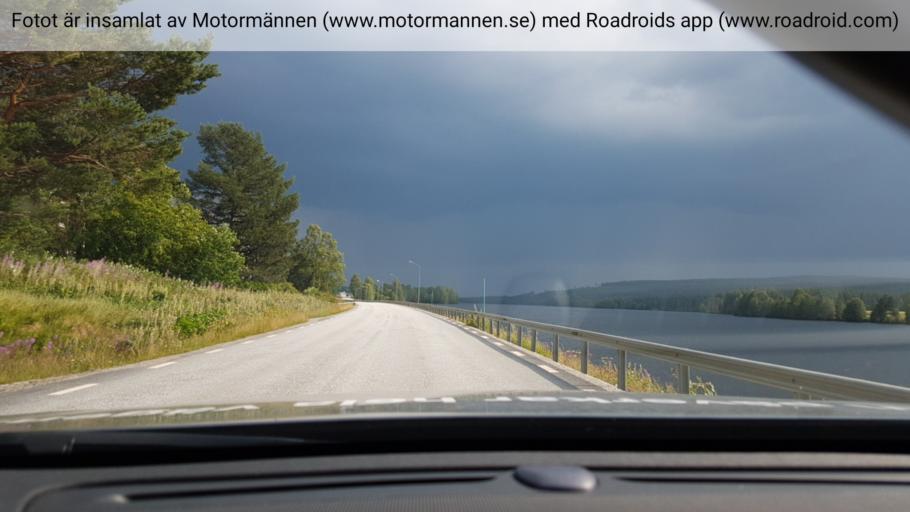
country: SE
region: Vaesterbotten
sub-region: Vindelns Kommun
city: Vindeln
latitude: 64.1773
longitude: 19.4799
